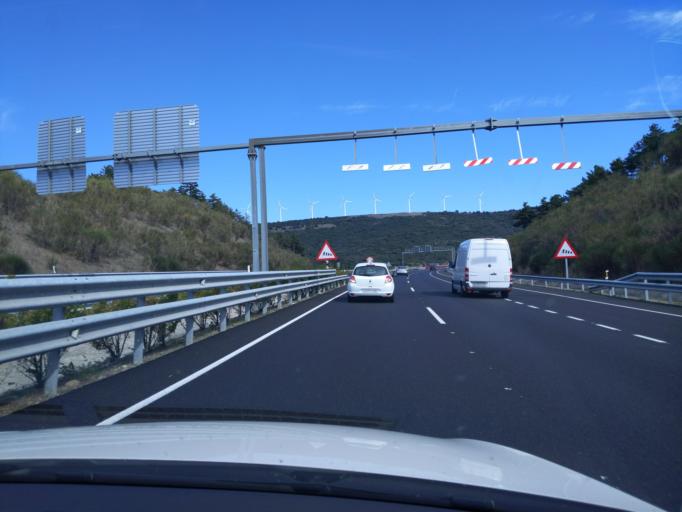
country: ES
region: Navarre
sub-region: Provincia de Navarra
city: Legarda
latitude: 42.7280
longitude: -1.7612
